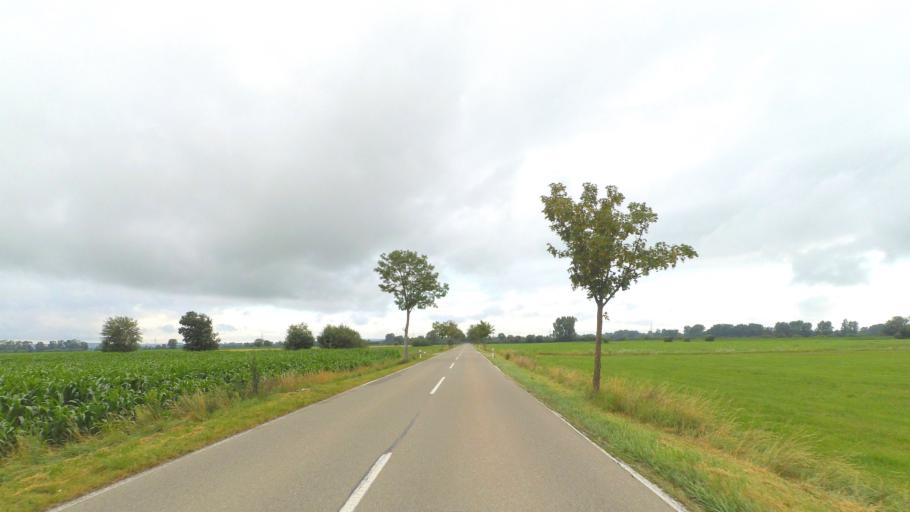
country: DE
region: Baden-Wuerttemberg
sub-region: Tuebingen Region
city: Rammingen
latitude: 48.4658
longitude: 10.1655
